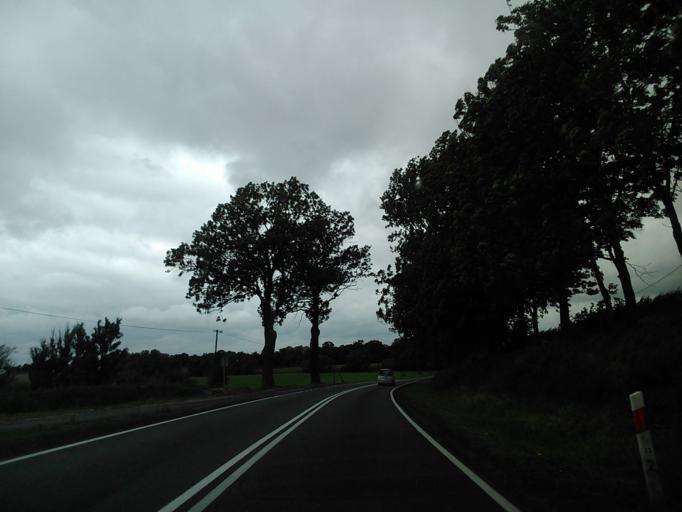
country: PL
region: Kujawsko-Pomorskie
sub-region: Powiat radziejowski
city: Piotrkow Kujawski
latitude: 52.6142
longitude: 18.4166
